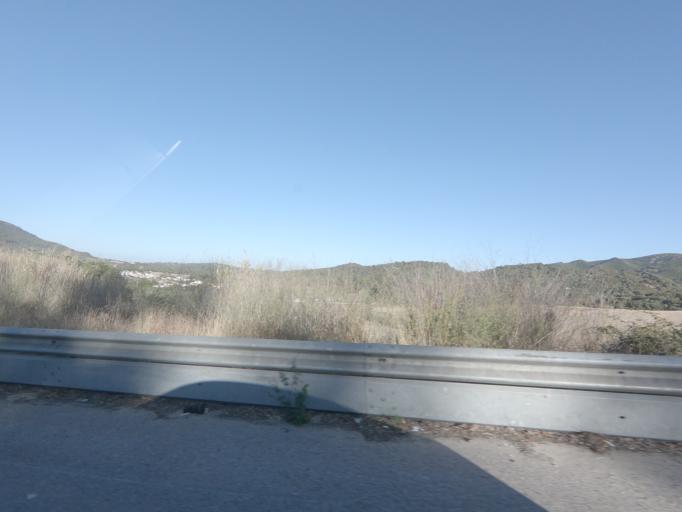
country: PT
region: Setubal
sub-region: Palmela
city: Quinta do Anjo
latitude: 38.5167
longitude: -8.9758
